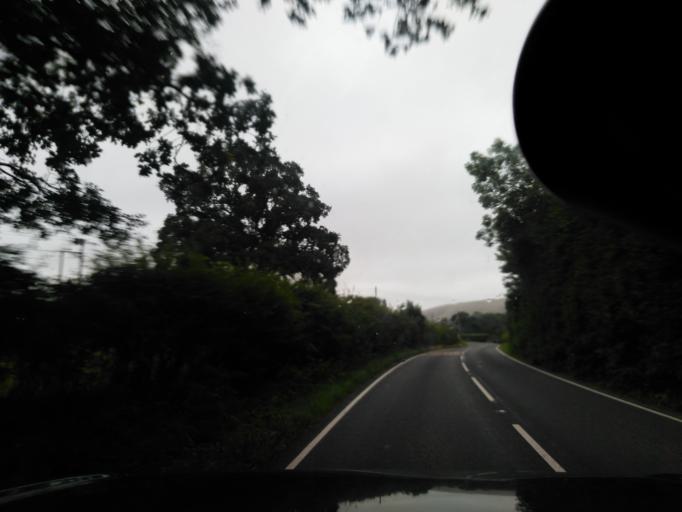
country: GB
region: England
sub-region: Dorset
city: Shaftesbury
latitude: 50.9583
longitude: -2.1914
